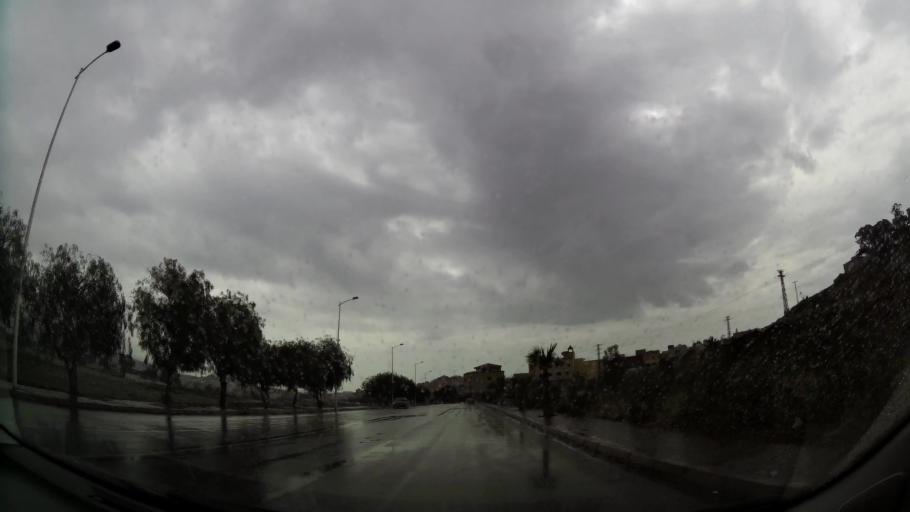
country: MA
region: Oriental
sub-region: Nador
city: Nador
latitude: 35.1459
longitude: -3.0096
